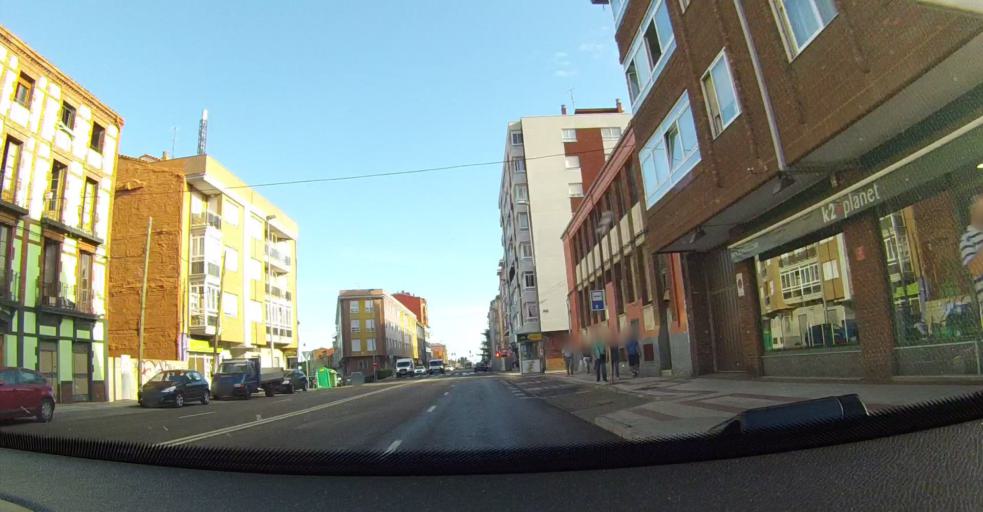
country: ES
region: Castille and Leon
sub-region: Provincia de Leon
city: Leon
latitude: 42.5985
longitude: -5.5857
